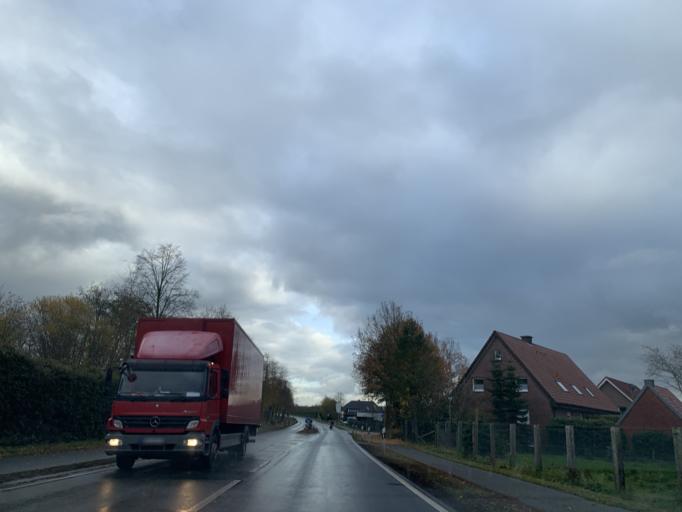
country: DE
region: North Rhine-Westphalia
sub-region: Regierungsbezirk Munster
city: Steinfurt
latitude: 52.1161
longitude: 7.3768
